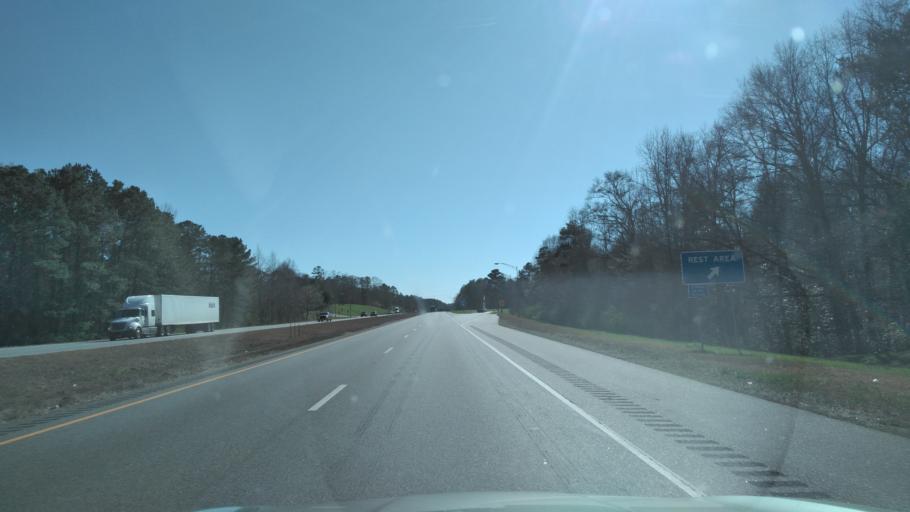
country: US
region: Alabama
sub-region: Butler County
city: Greenville
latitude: 31.8872
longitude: -86.6071
